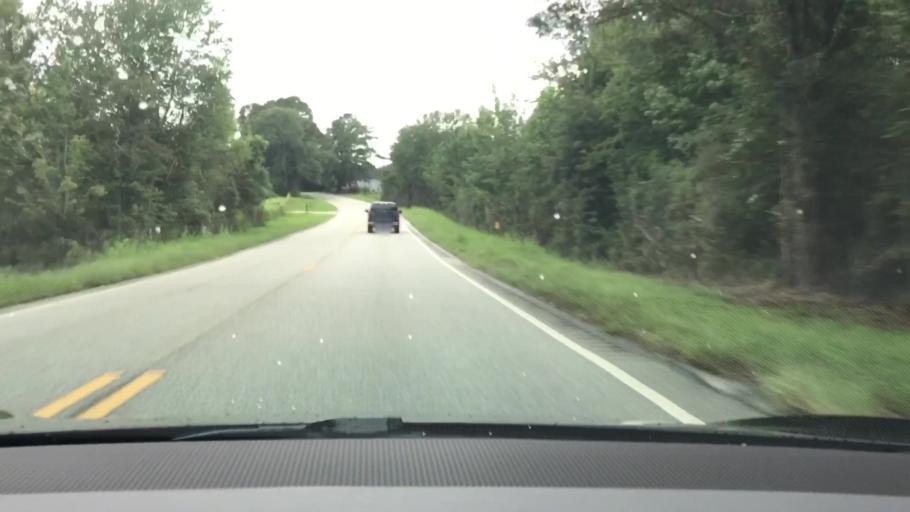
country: US
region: Alabama
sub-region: Geneva County
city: Samson
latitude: 31.0031
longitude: -86.1307
